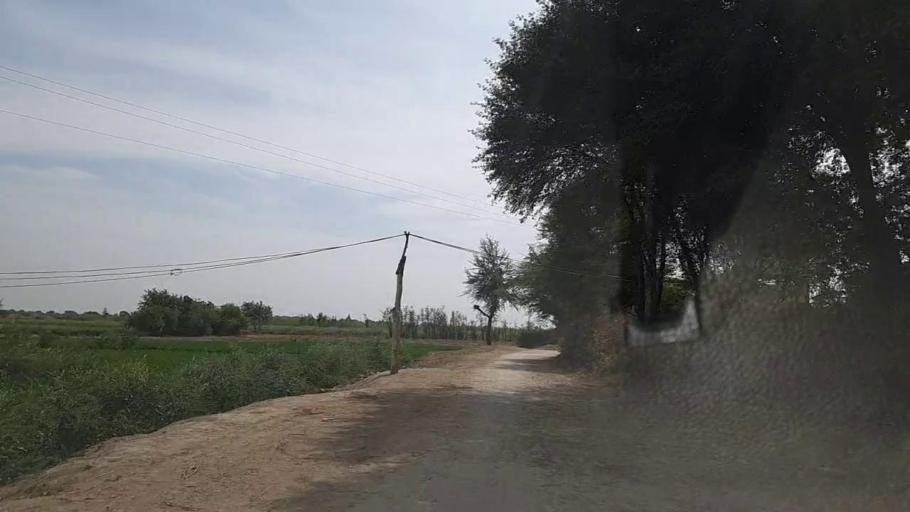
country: PK
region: Sindh
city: Kunri
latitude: 25.2097
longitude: 69.4930
